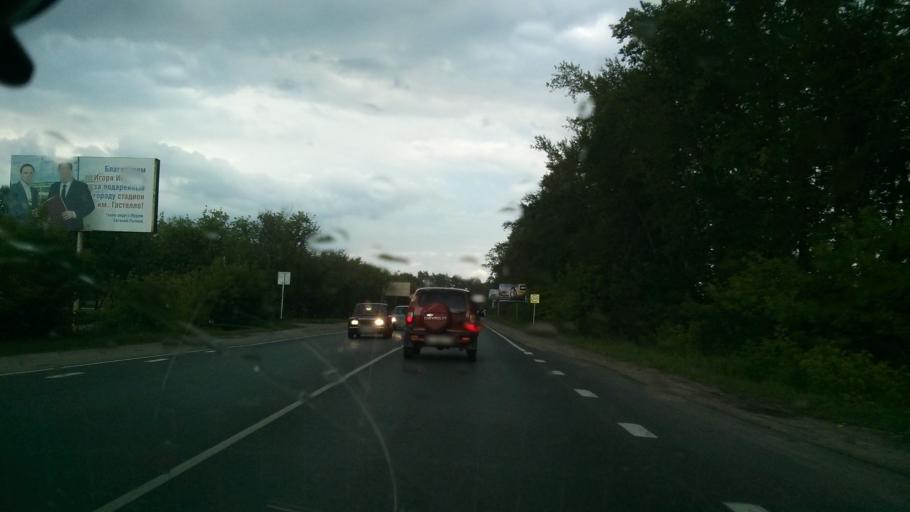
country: RU
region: Vladimir
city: Murom
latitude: 55.6010
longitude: 42.0306
